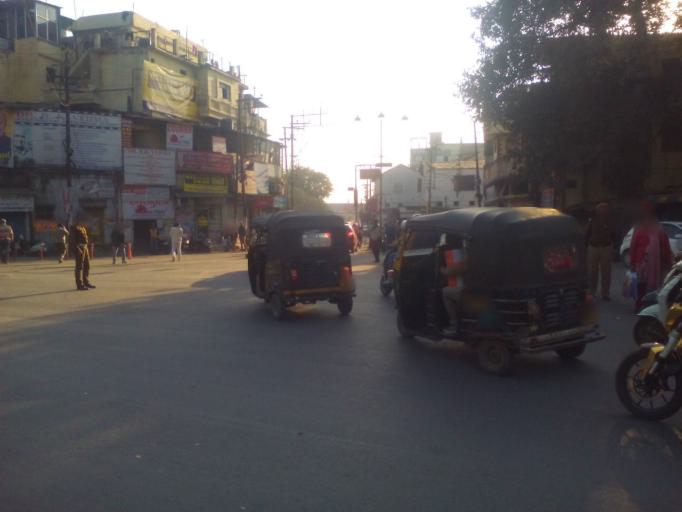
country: IN
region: Uttarakhand
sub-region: Dehradun
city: Dehradun
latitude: 30.3241
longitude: 78.0421
